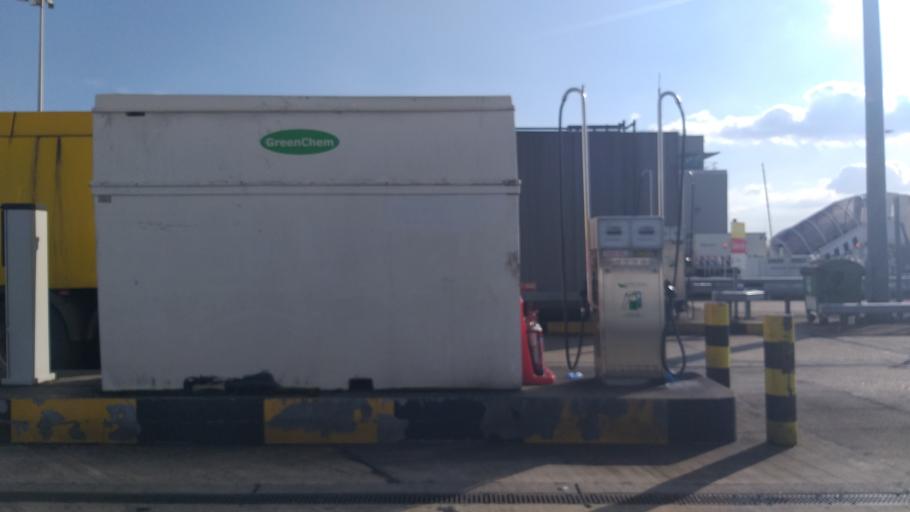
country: GB
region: England
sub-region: Greater London
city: West Drayton
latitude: 51.4705
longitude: -0.4708
